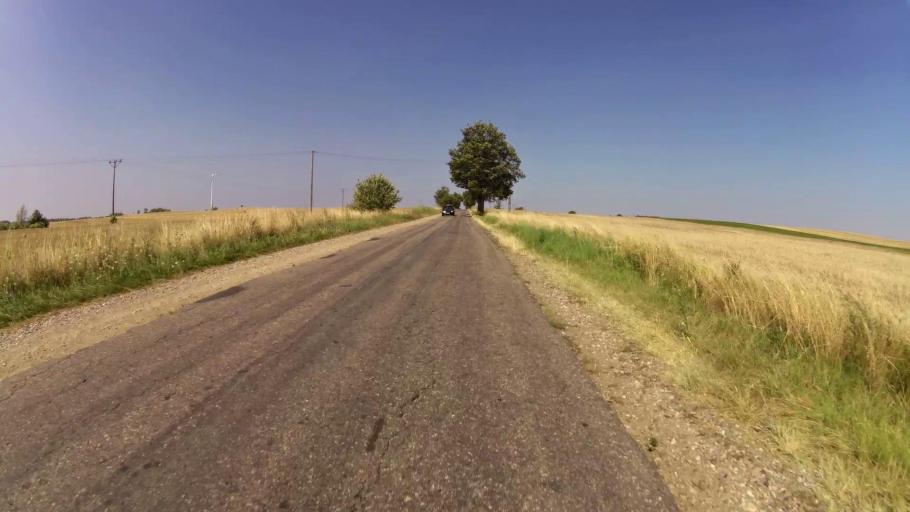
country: PL
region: West Pomeranian Voivodeship
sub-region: Powiat walecki
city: Walcz
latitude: 53.2162
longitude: 16.4757
